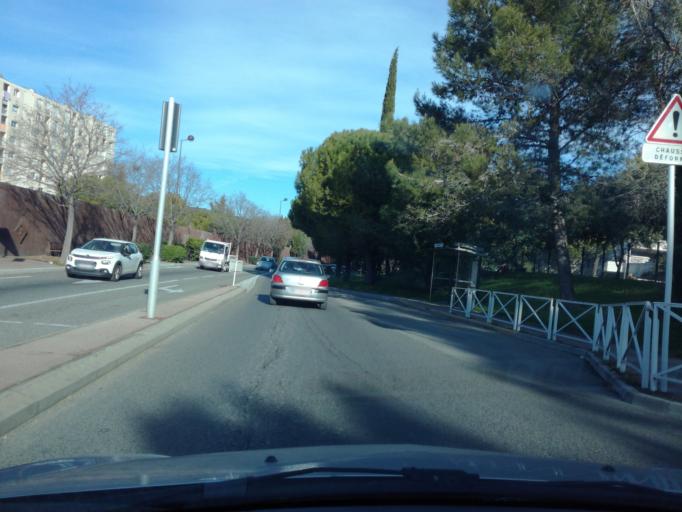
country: FR
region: Provence-Alpes-Cote d'Azur
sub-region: Departement des Alpes-Maritimes
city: Vallauris
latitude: 43.5765
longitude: 7.0903
